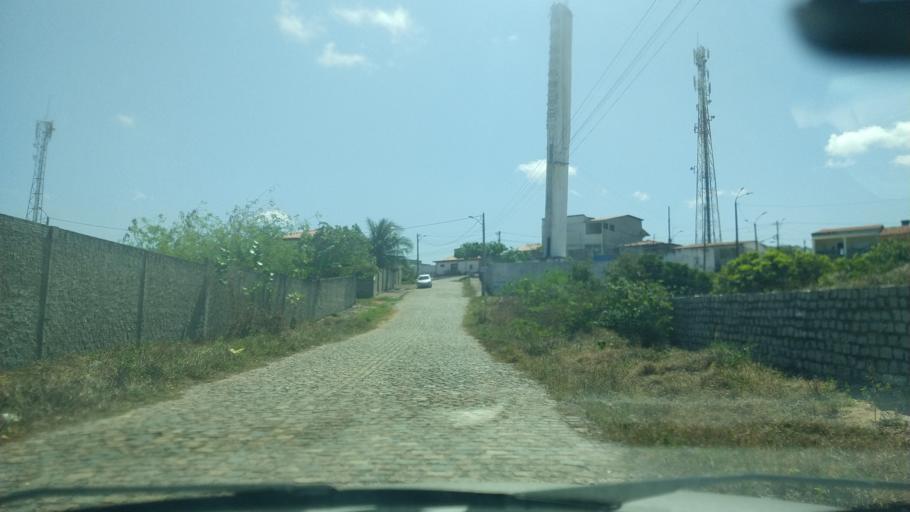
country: BR
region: Rio Grande do Norte
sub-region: Parnamirim
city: Parnamirim
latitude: -5.9474
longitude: -35.1556
